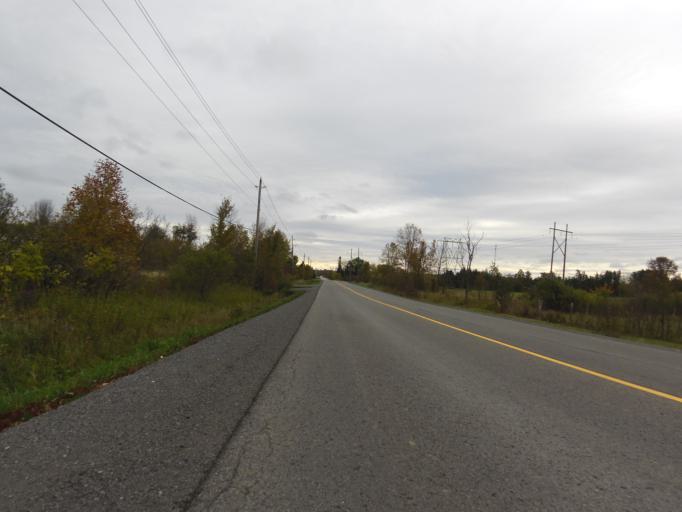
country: CA
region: Ontario
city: Bells Corners
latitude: 45.4069
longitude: -76.0750
